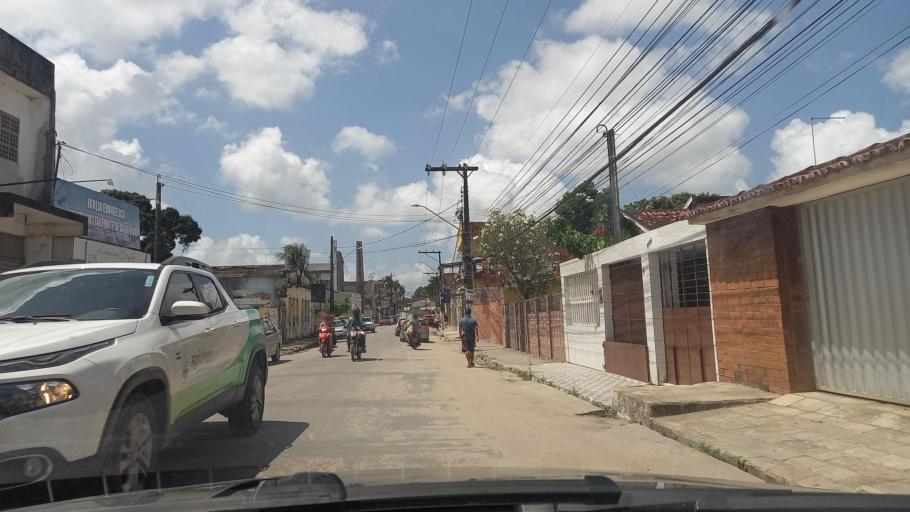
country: BR
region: Pernambuco
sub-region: Goiana
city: Goiana
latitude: -7.5622
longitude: -35.0036
